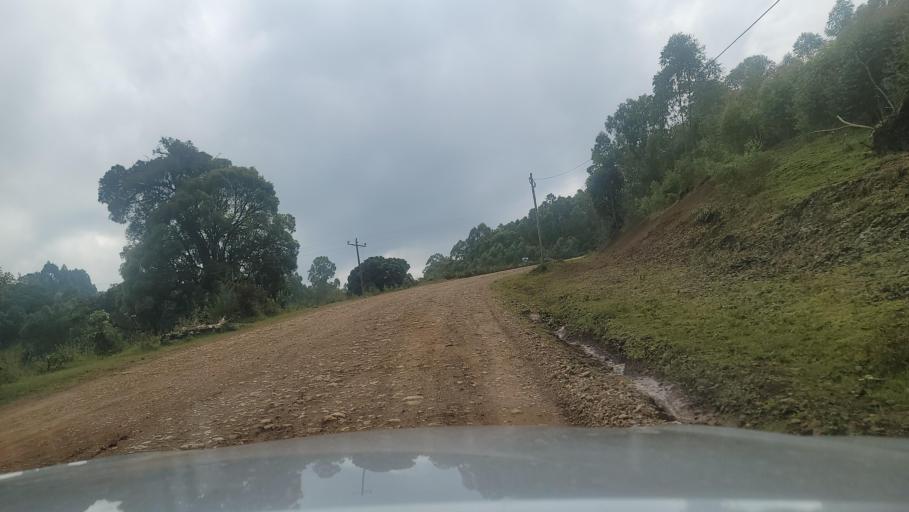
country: ET
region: Oromiya
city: Agaro
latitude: 7.7959
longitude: 36.4548
